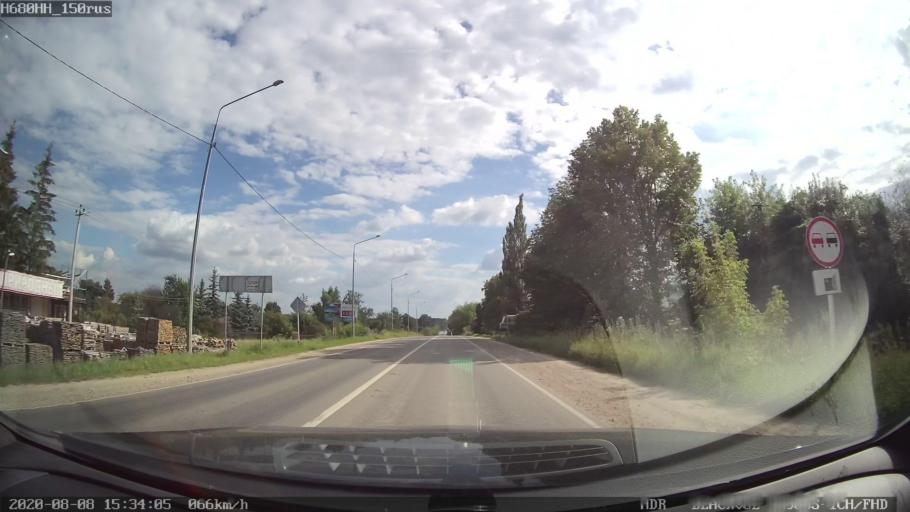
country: RU
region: Tula
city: Zaokskiy
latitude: 54.7646
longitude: 37.4367
